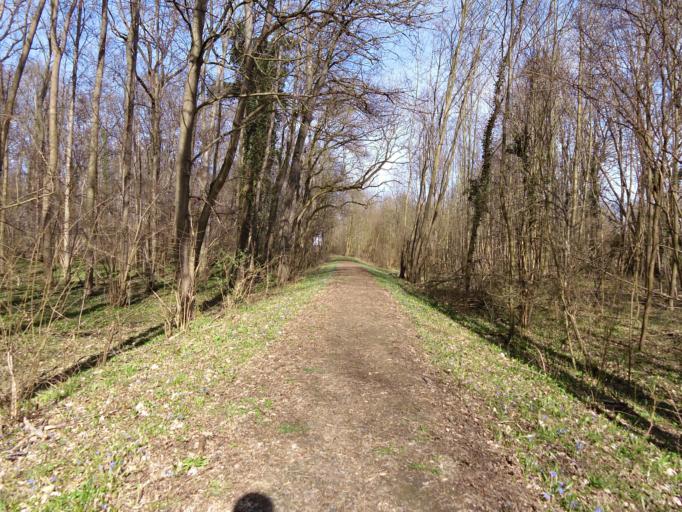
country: DE
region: Hesse
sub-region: Regierungsbezirk Darmstadt
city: Stockstadt am Rhein
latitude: 49.8237
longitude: 8.4160
